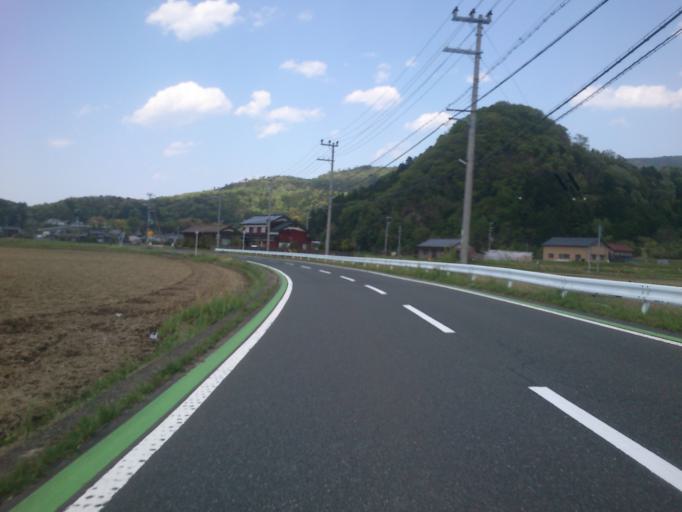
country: JP
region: Kyoto
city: Miyazu
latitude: 35.7176
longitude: 135.1079
